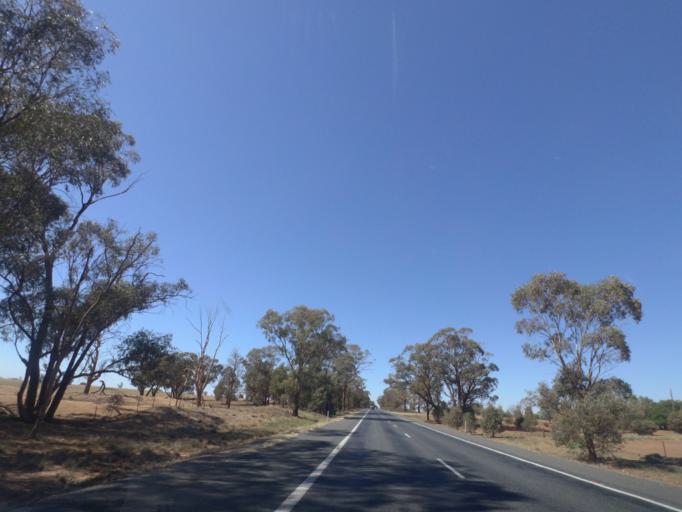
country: AU
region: New South Wales
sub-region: Bland
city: West Wyalong
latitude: -34.2065
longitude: 147.1095
